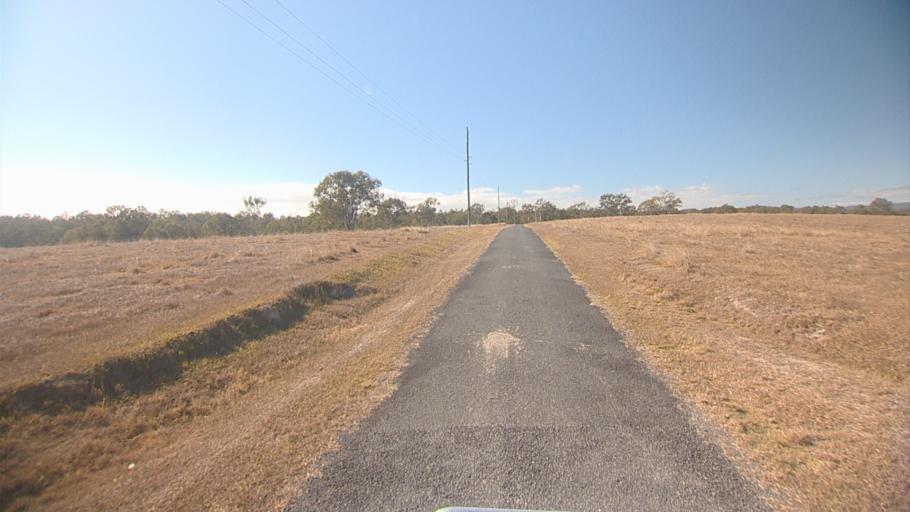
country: AU
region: Queensland
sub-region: Logan
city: North Maclean
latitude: -27.8023
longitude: 153.0201
